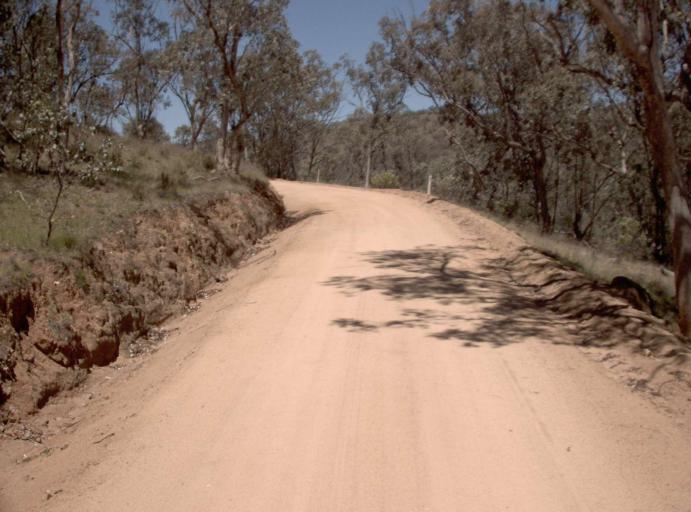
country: AU
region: New South Wales
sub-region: Snowy River
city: Jindabyne
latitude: -36.9336
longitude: 148.3581
